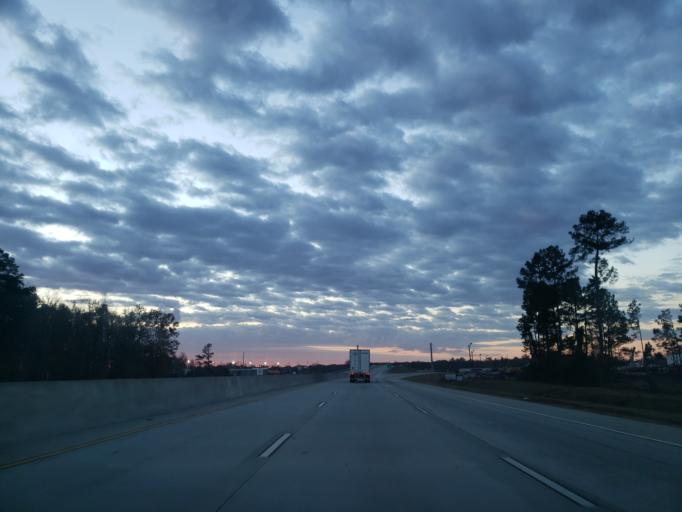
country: US
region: Georgia
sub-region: Chatham County
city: Port Wentworth
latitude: 32.1404
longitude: -81.1683
